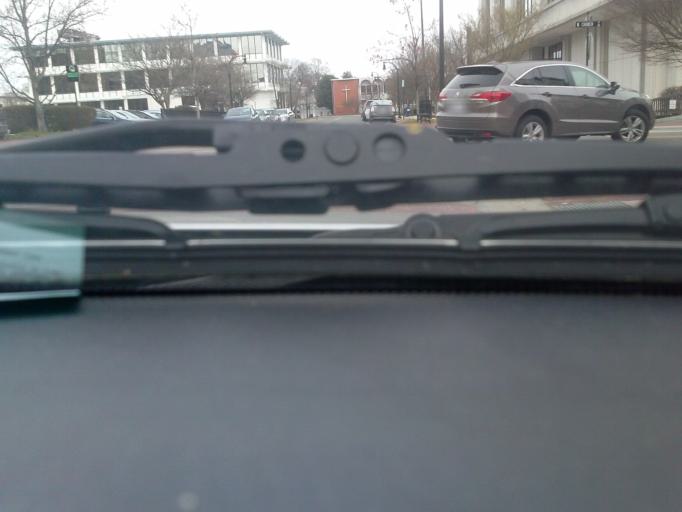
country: US
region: North Carolina
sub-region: Durham County
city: Durham
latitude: 35.9950
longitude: -78.8992
